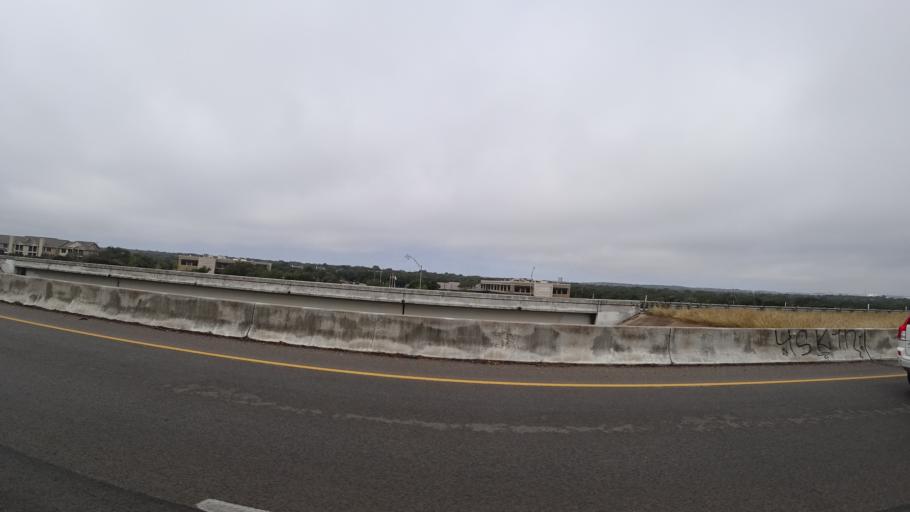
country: US
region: Texas
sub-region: Travis County
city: Shady Hollow
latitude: 30.2080
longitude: -97.8609
